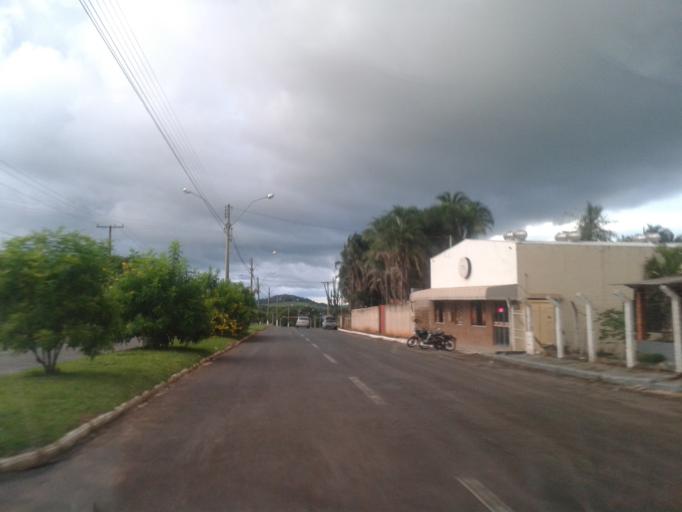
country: BR
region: Goias
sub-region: Morrinhos
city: Morrinhos
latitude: -17.7302
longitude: -49.1491
